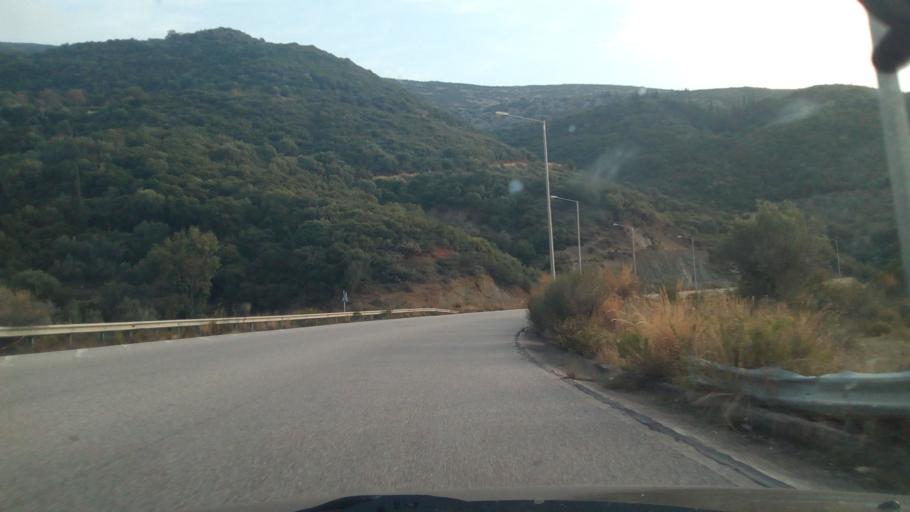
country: GR
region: West Greece
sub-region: Nomos Aitolias kai Akarnanias
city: Nafpaktos
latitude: 38.4029
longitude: 21.8057
